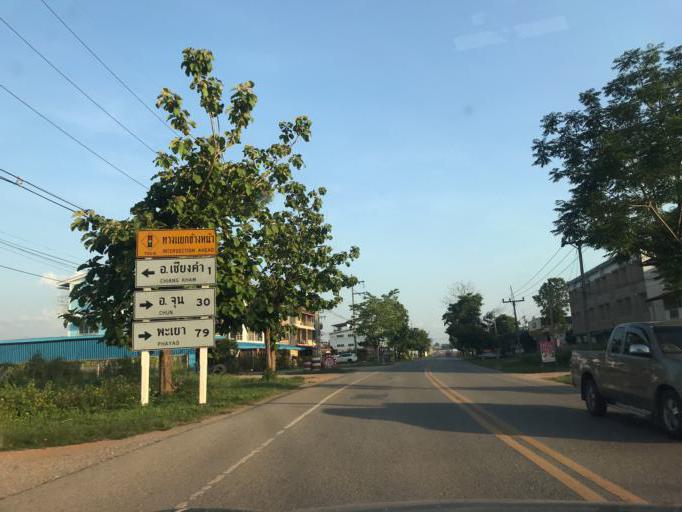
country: TH
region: Phayao
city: Chiang Kham
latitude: 19.5245
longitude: 100.2950
